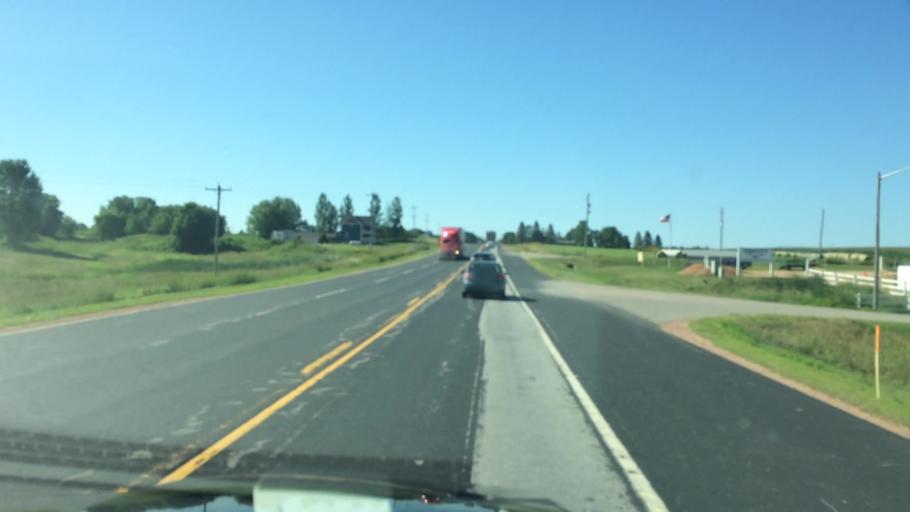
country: US
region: Wisconsin
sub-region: Marathon County
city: Stratford
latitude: 44.8201
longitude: -90.0791
